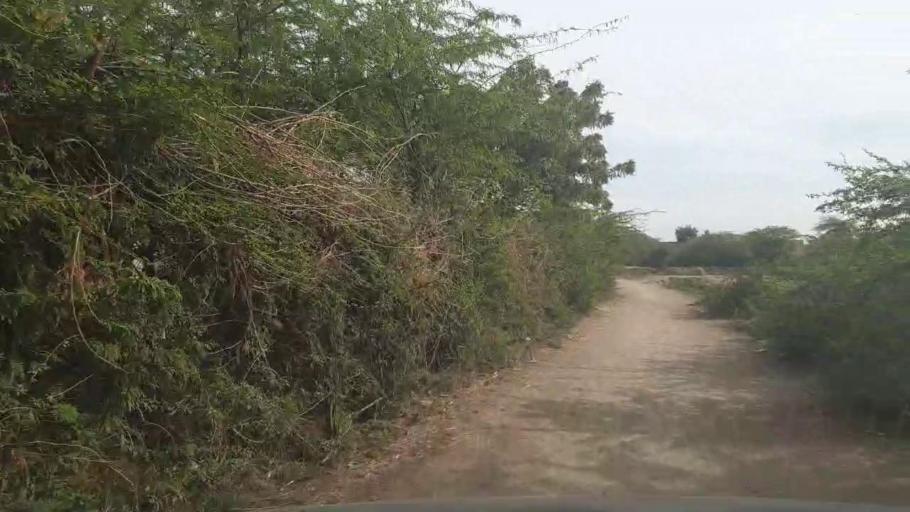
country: PK
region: Sindh
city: Kunri
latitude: 25.2965
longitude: 69.5890
